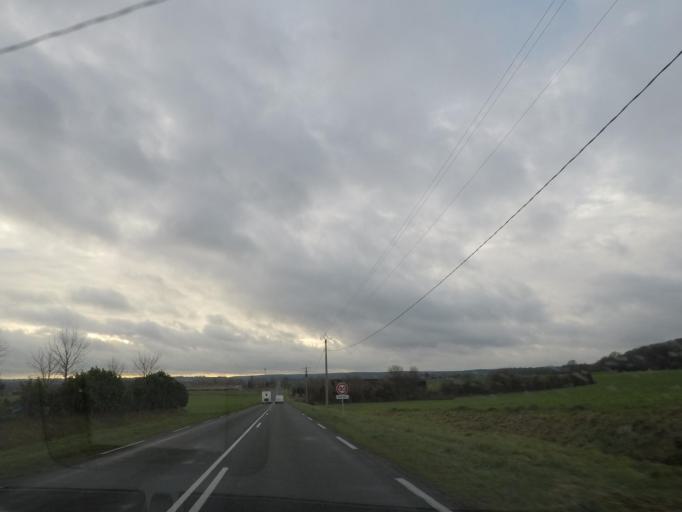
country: FR
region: Pays de la Loire
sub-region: Departement de la Sarthe
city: Vibraye
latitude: 48.0937
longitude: 0.7214
